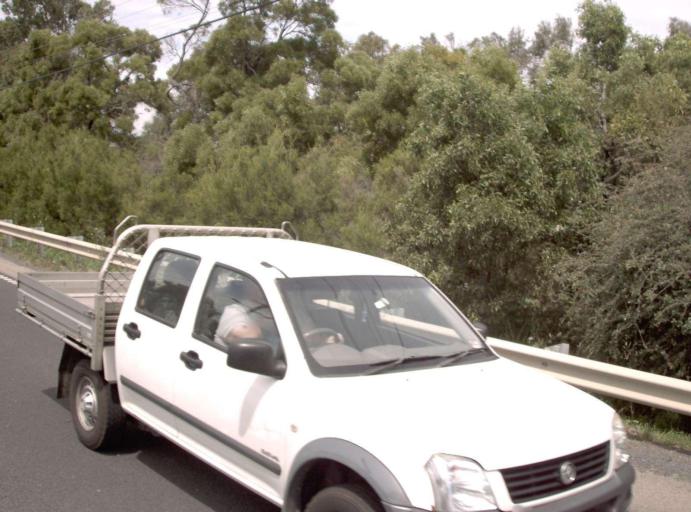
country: AU
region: Victoria
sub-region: Mornington Peninsula
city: Hastings
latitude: -38.2819
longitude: 145.1888
